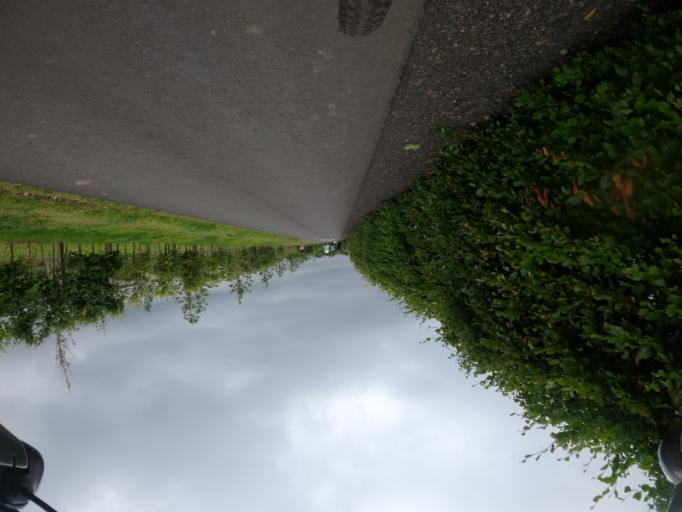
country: GB
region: Scotland
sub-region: Edinburgh
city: Colinton
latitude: 55.9025
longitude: -3.2794
